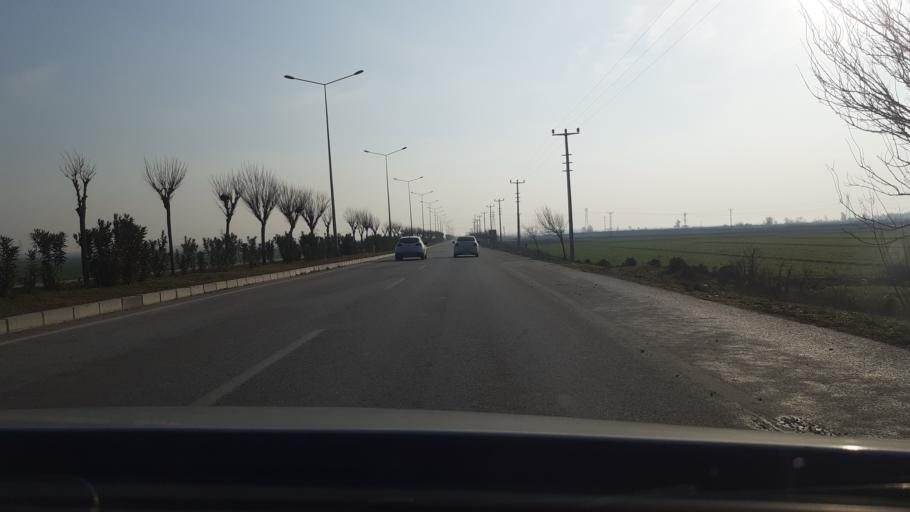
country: TR
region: Hatay
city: Serinyol
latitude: 36.3717
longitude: 36.2364
